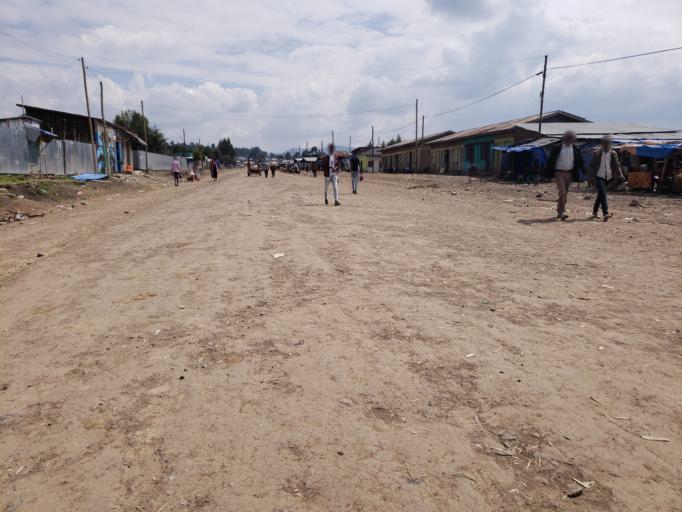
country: ET
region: Oromiya
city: Dodola
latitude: 7.0051
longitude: 39.3917
